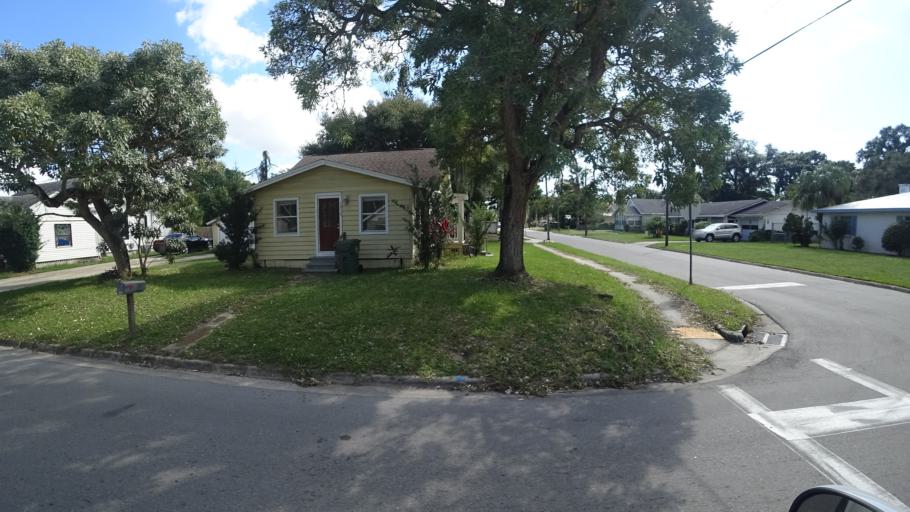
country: US
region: Florida
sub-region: Manatee County
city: Bradenton
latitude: 27.4872
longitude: -82.5771
